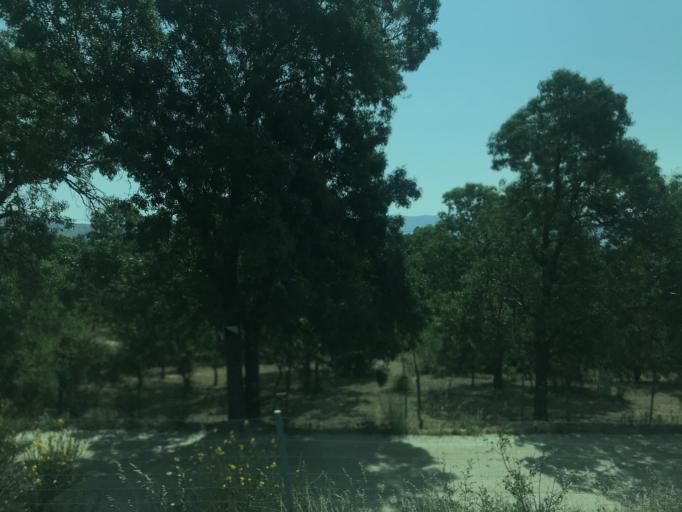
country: ES
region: Madrid
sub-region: Provincia de Madrid
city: Braojos
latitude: 41.0510
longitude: -3.6150
